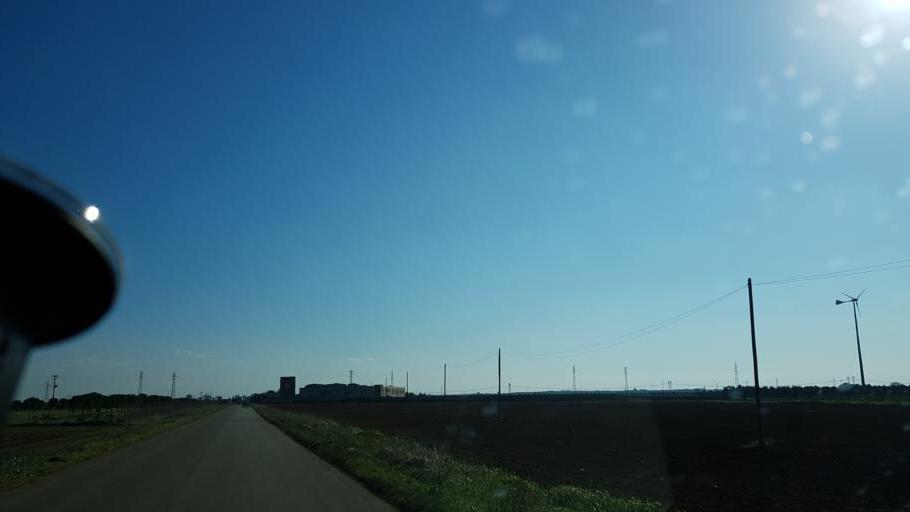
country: IT
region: Apulia
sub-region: Provincia di Brindisi
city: Brindisi
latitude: 40.6207
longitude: 17.8651
